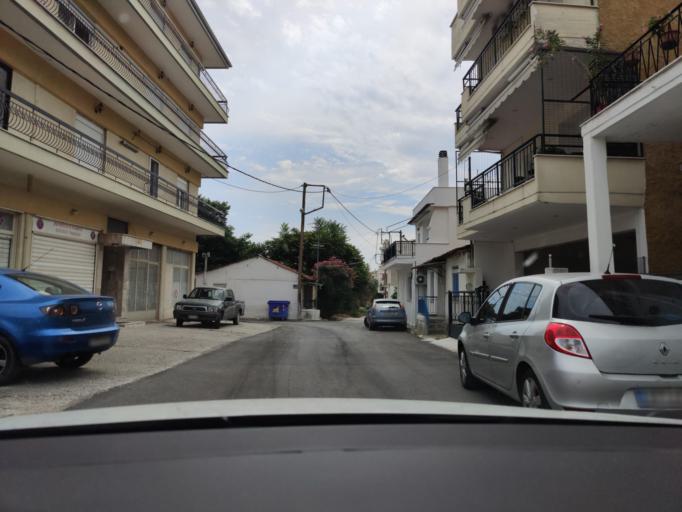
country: GR
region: Central Macedonia
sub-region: Nomos Serron
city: Serres
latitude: 41.0859
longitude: 23.5347
